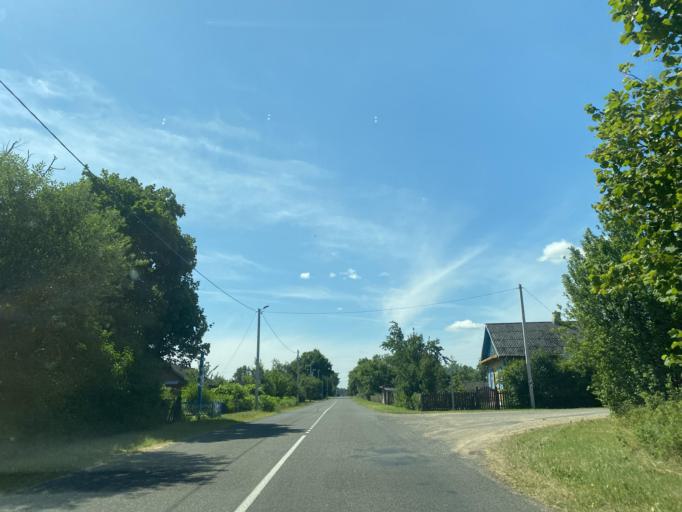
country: BY
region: Brest
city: Ivanava
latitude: 52.2027
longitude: 25.6151
